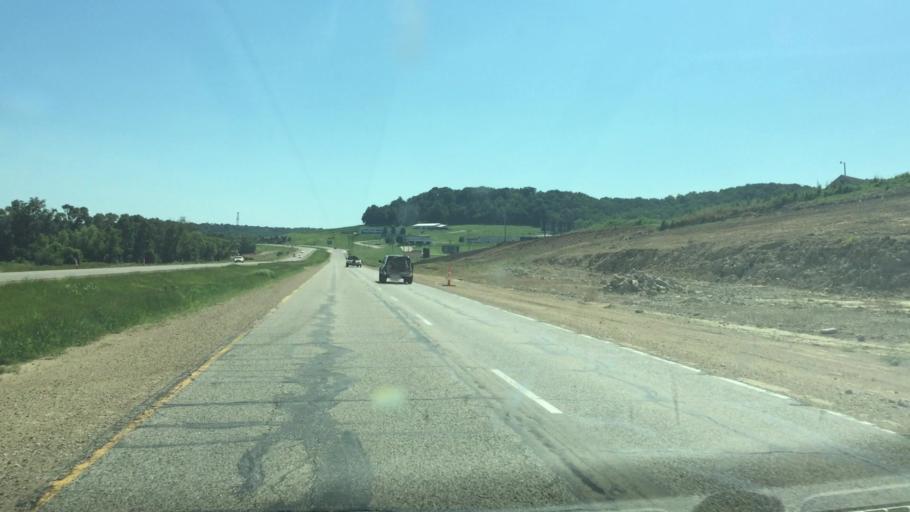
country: US
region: Iowa
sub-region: Dubuque County
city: Dubuque
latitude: 42.4334
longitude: -90.6844
